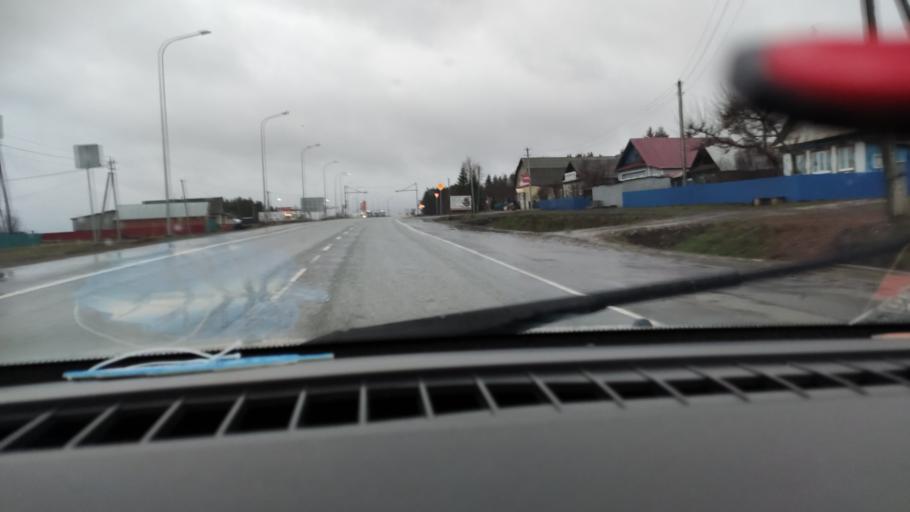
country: RU
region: Tatarstan
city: Mendeleyevsk
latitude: 56.0276
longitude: 52.3703
